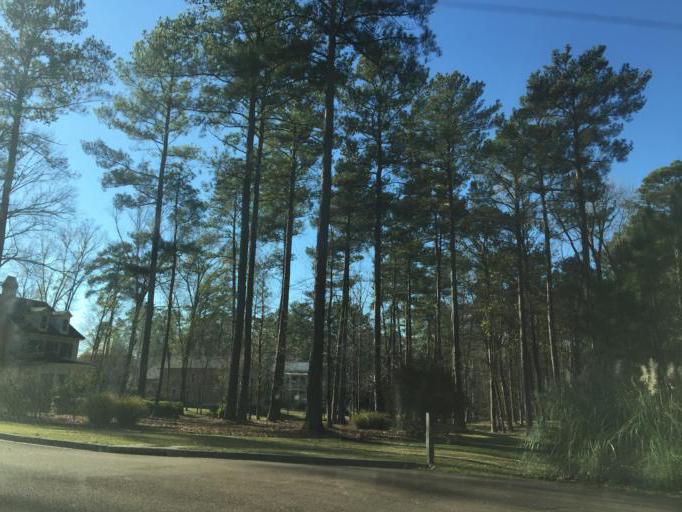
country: US
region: Mississippi
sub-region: Madison County
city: Madison
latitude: 32.4598
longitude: -90.0594
